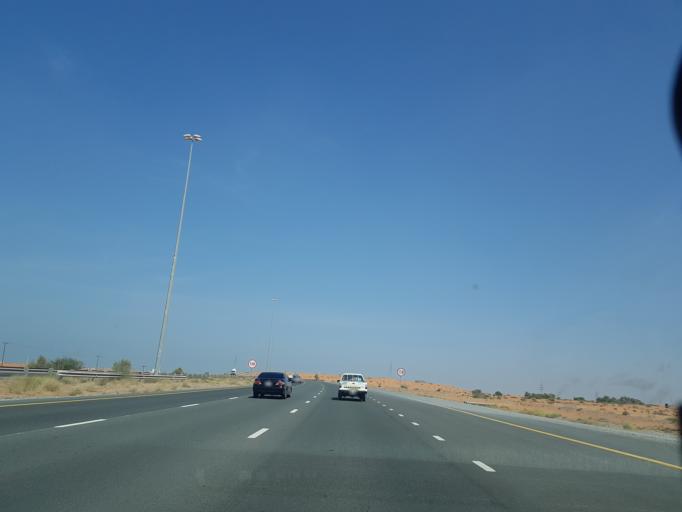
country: AE
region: Ra's al Khaymah
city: Ras al-Khaimah
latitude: 25.6753
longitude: 55.8829
